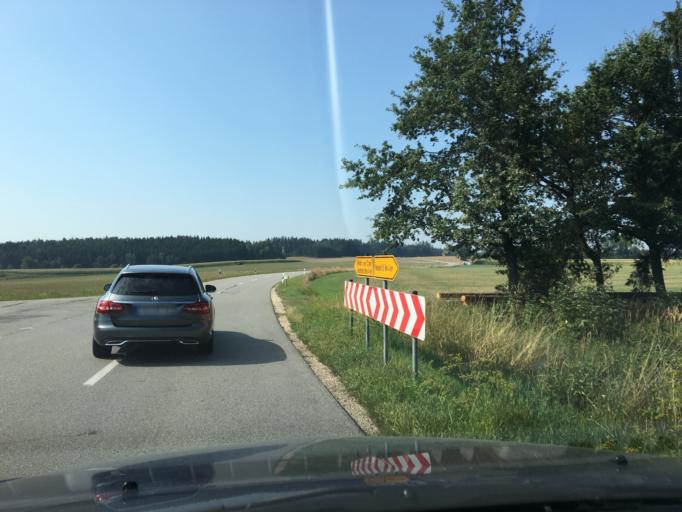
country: DE
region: Bavaria
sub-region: Upper Bavaria
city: Niederbergkirchen
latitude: 48.3287
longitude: 12.4821
